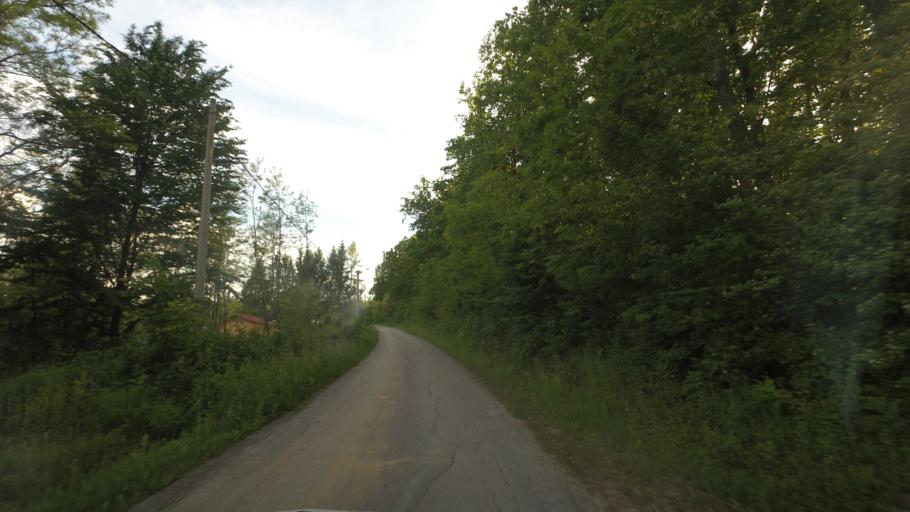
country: HR
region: Sisacko-Moslavacka
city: Gvozd
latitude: 45.3146
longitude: 15.9734
